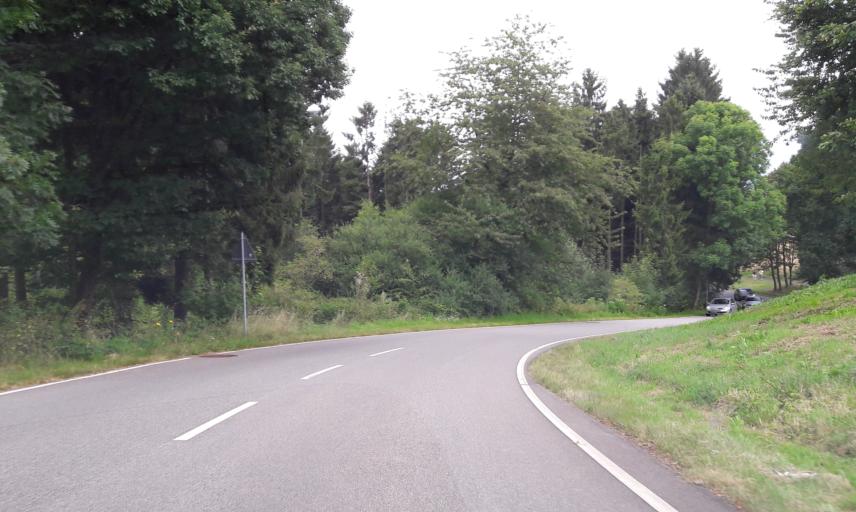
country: DE
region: Saarland
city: Tholey
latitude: 49.4899
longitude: 7.0323
